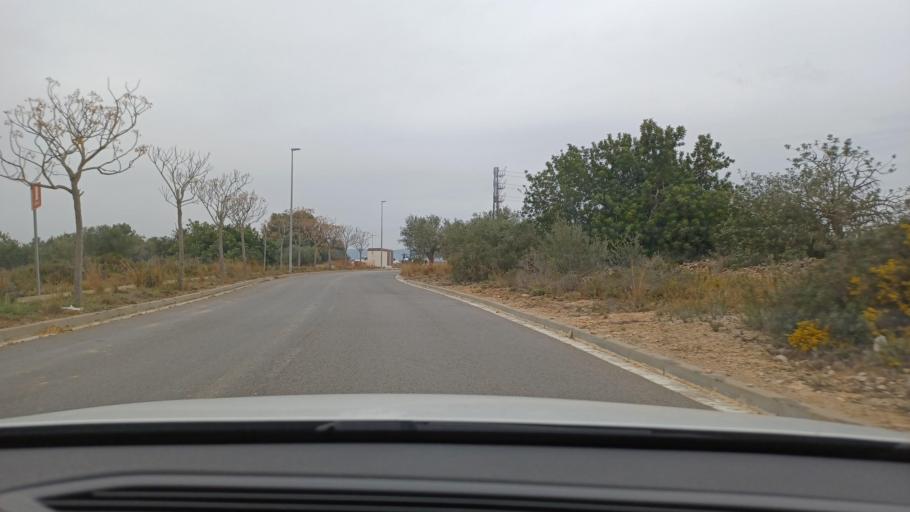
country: ES
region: Catalonia
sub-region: Provincia de Tarragona
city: Amposta
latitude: 40.7625
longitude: 0.5995
